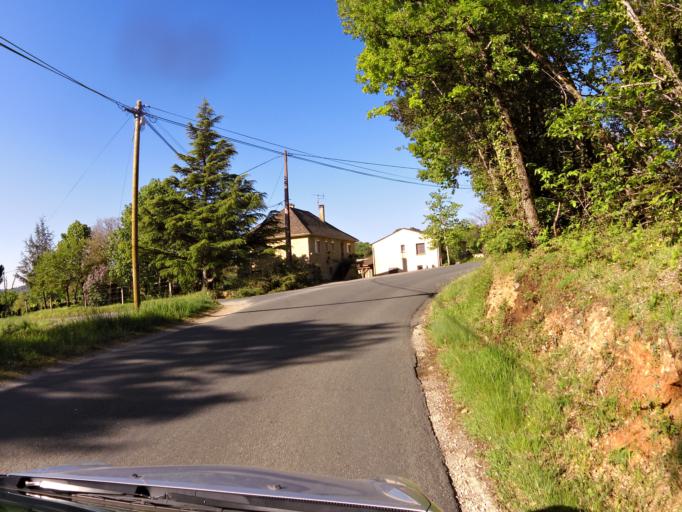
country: FR
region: Aquitaine
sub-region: Departement de la Dordogne
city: Carsac-Aillac
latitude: 44.8087
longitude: 1.2731
